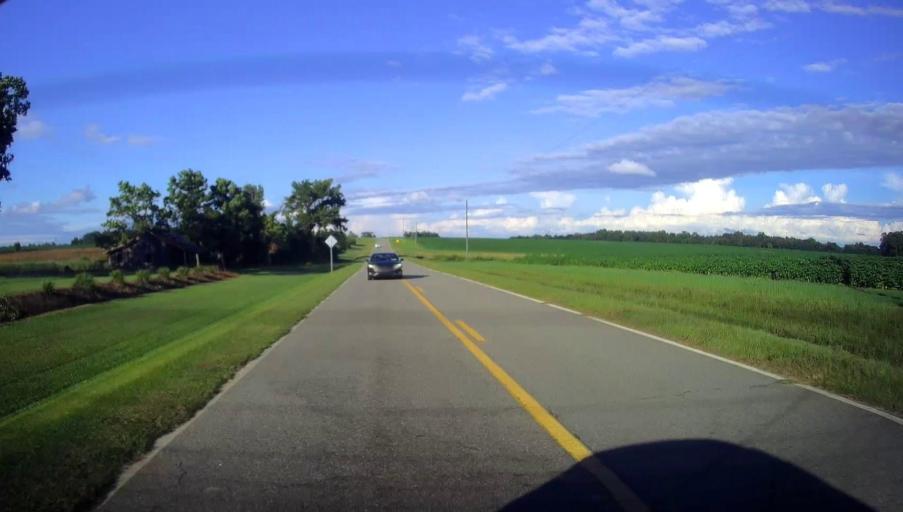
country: US
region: Georgia
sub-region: Bleckley County
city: Cochran
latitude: 32.4017
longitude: -83.4252
